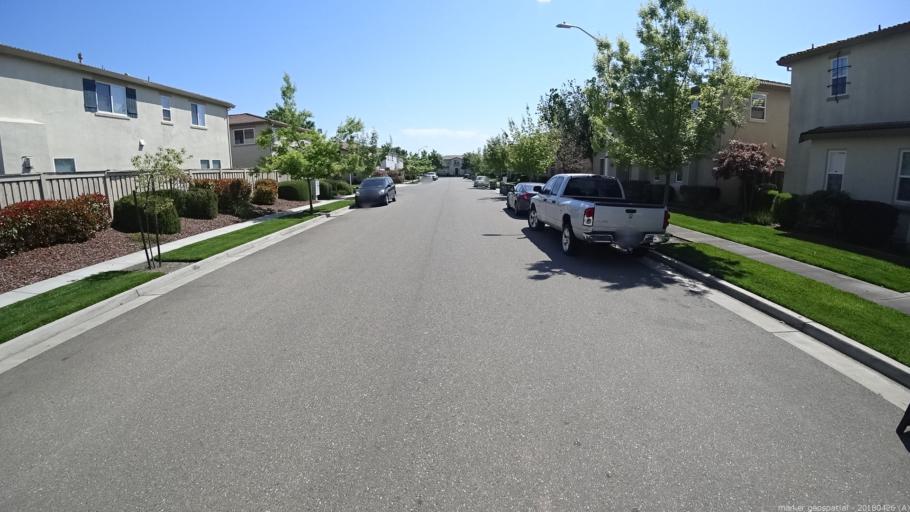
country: US
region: California
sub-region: Yolo County
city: West Sacramento
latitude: 38.5242
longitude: -121.5692
